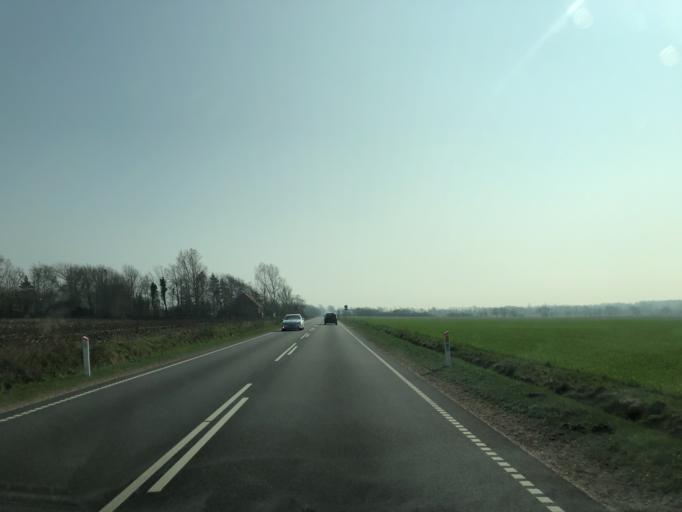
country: DK
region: Central Jutland
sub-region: Ringkobing-Skjern Kommune
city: Skjern
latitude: 55.9881
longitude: 8.5067
